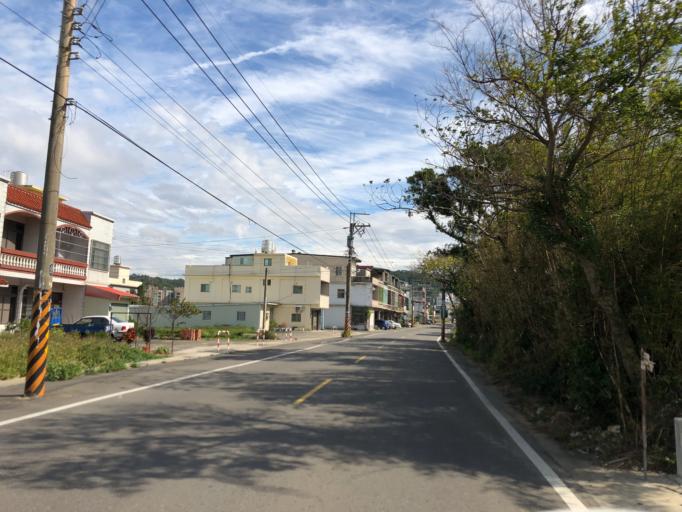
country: TW
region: Taiwan
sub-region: Hsinchu
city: Zhubei
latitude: 24.7904
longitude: 121.0649
